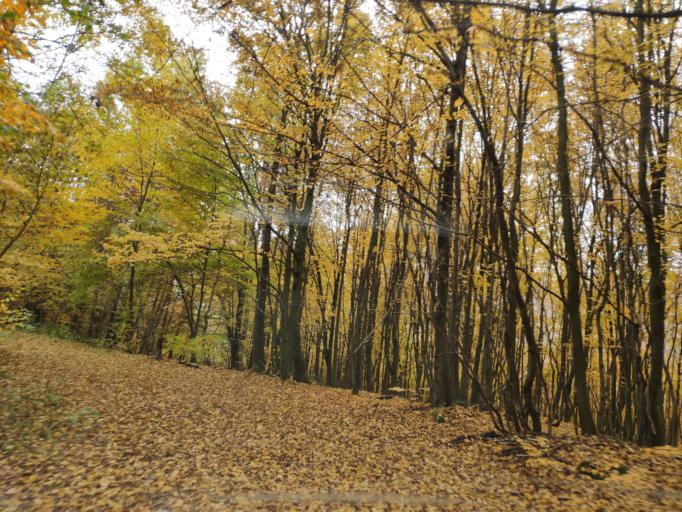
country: SK
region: Kosicky
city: Moldava nad Bodvou
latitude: 48.7263
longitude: 21.0929
